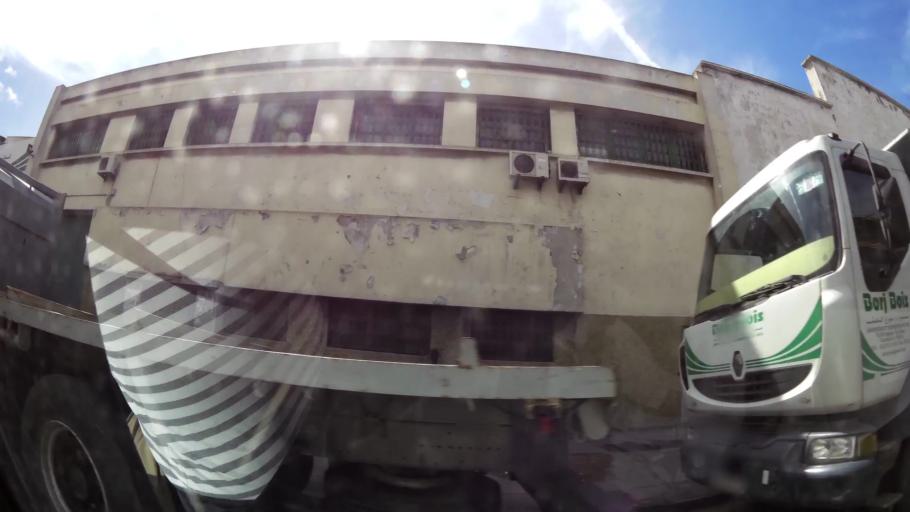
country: MA
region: Grand Casablanca
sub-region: Casablanca
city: Casablanca
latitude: 33.5815
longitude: -7.5838
